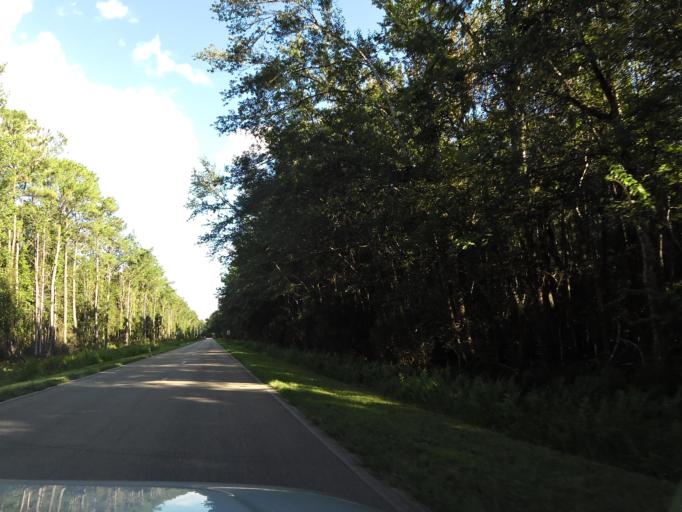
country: US
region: Florida
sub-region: Wakulla County
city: Crawfordville
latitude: 30.0670
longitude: -84.5040
